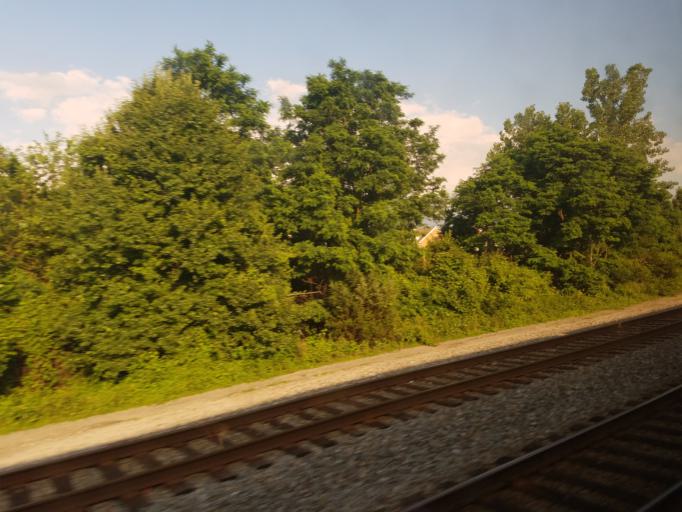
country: US
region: Virginia
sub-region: City of Alexandria
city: Alexandria
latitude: 38.8296
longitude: -77.0471
